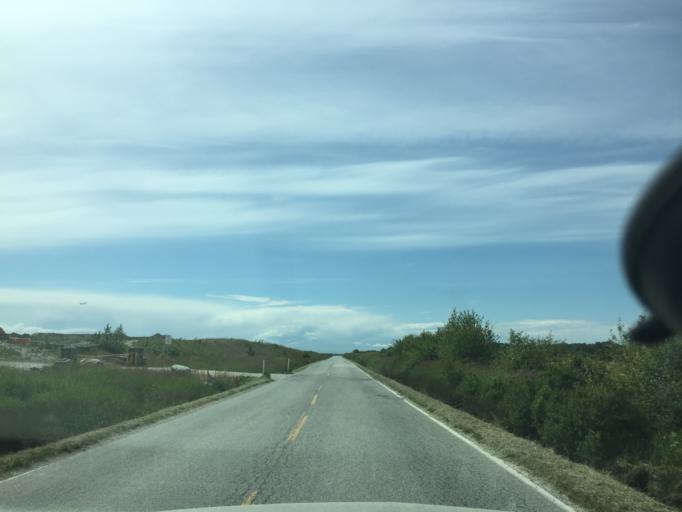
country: CA
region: British Columbia
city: Richmond
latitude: 49.2067
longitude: -123.1810
